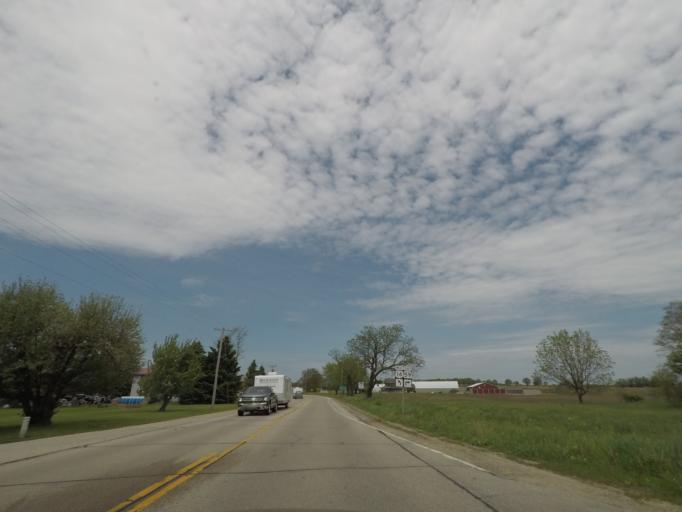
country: US
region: Wisconsin
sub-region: Rock County
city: Evansville
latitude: 42.8242
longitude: -89.3023
